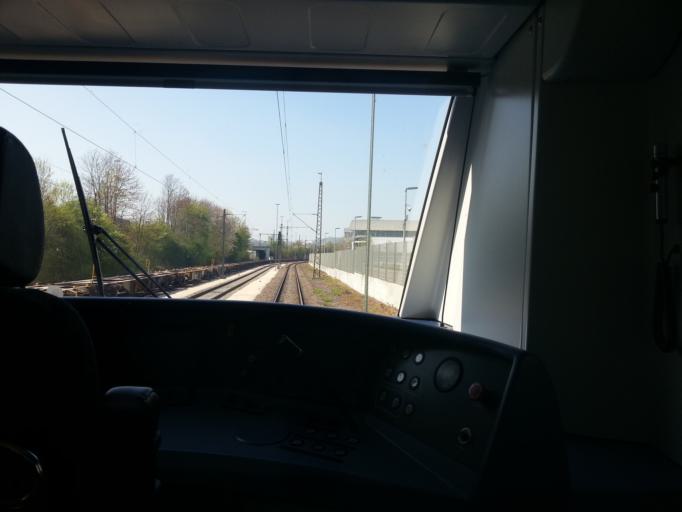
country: DE
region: Baden-Wuerttemberg
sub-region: Regierungsbezirk Stuttgart
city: Stuttgart-Ost
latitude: 48.7945
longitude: 9.2364
